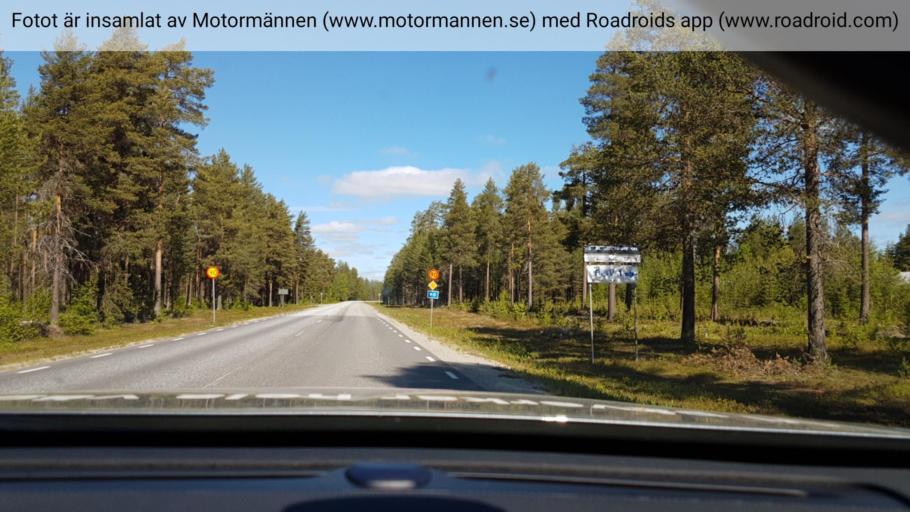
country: SE
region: Vaesterbotten
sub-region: Asele Kommun
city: Asele
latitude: 64.1736
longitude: 17.3616
